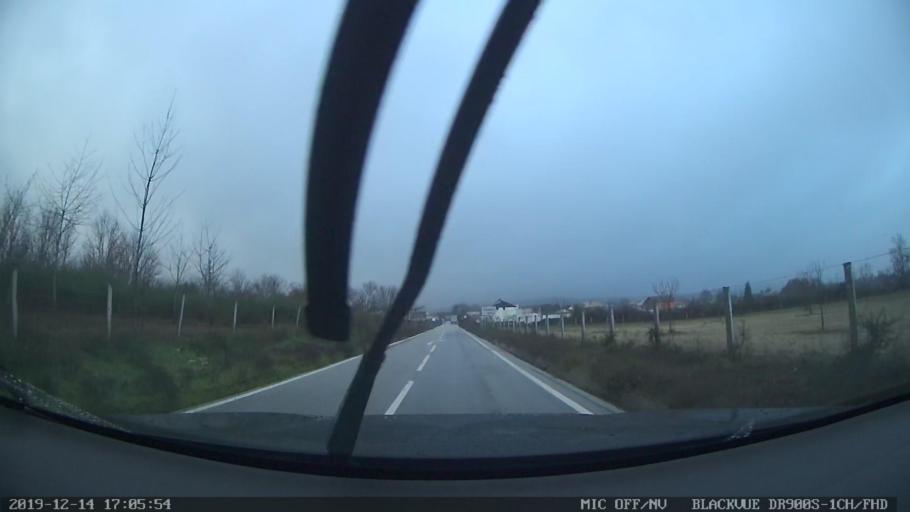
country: PT
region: Vila Real
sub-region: Vila Pouca de Aguiar
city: Vila Pouca de Aguiar
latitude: 41.4536
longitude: -7.5882
